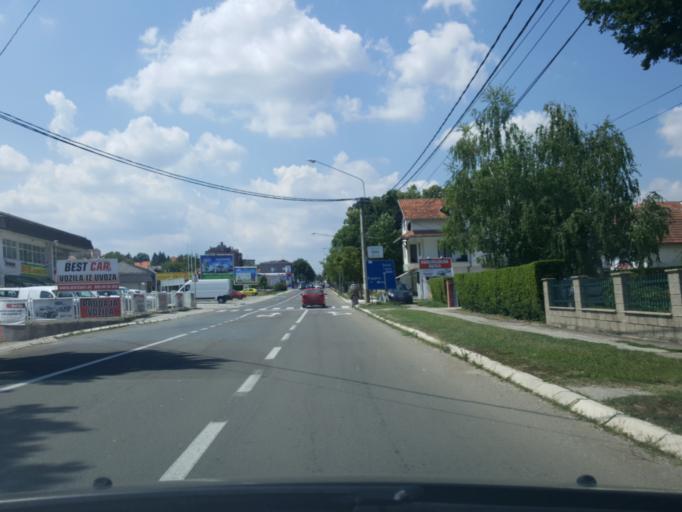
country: RS
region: Central Serbia
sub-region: Sumadijski Okrug
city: Topola
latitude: 44.2592
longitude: 20.6846
